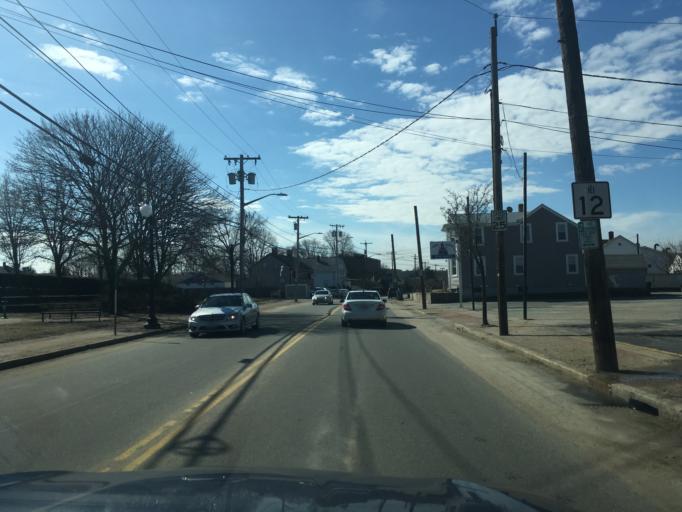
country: US
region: Rhode Island
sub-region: Providence County
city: Cranston
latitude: 41.7827
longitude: -71.4651
